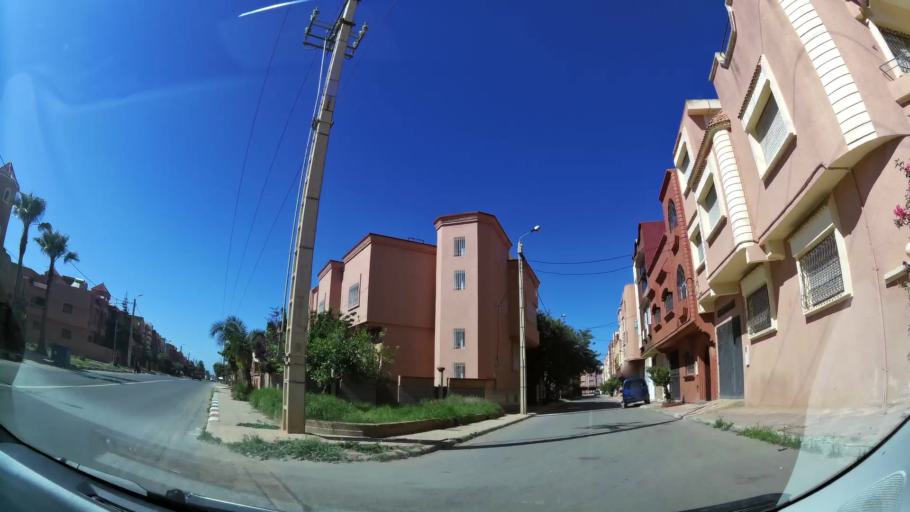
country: MA
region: Oriental
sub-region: Berkane-Taourirt
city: Berkane
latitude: 34.9373
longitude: -2.3239
